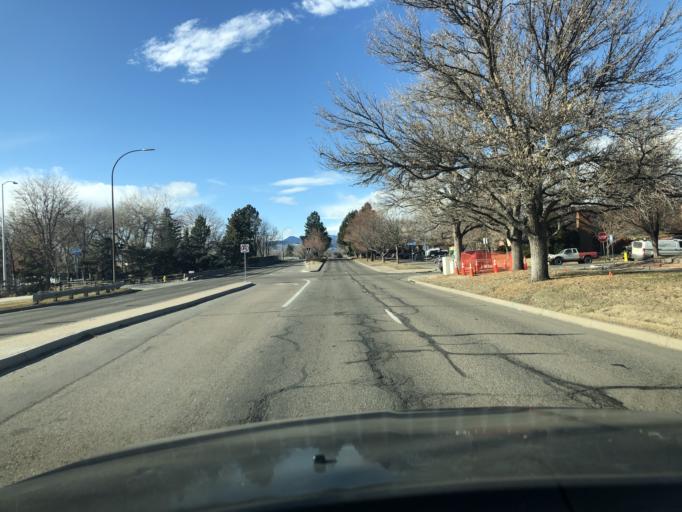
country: US
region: Colorado
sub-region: Jefferson County
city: Arvada
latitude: 39.8018
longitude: -105.1302
